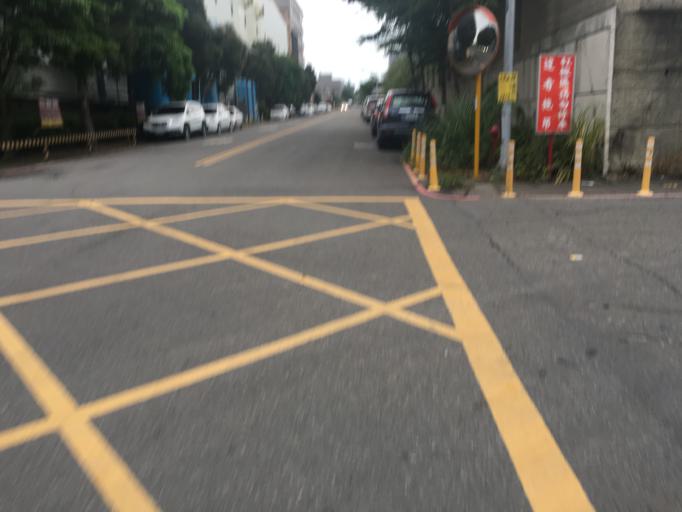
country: TW
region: Taiwan
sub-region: Hsinchu
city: Hsinchu
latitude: 24.7274
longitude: 120.9111
